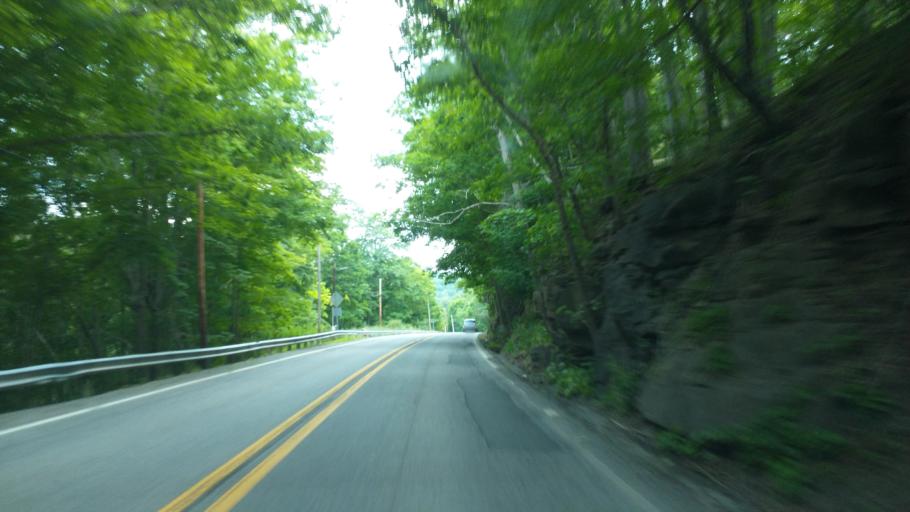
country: US
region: West Virginia
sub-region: Mercer County
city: Athens
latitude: 37.4433
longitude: -81.0016
